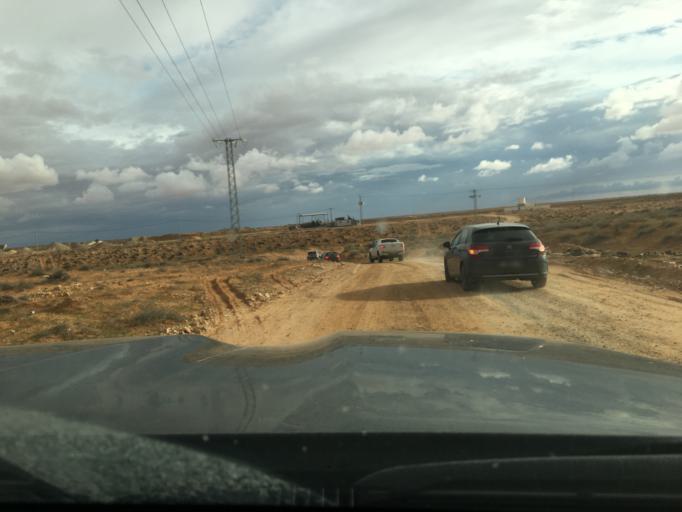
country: TN
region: Madanin
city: Medenine
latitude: 33.2691
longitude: 10.5688
